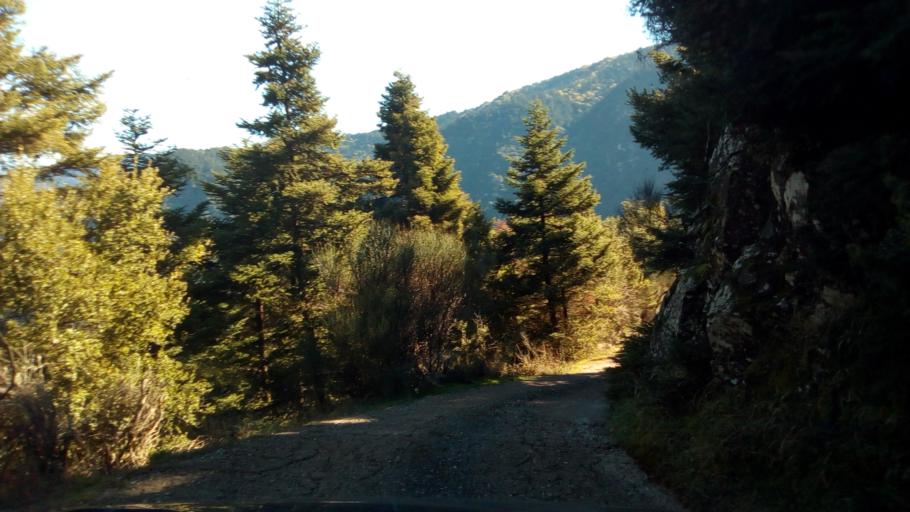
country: GR
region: West Greece
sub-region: Nomos Aitolias kai Akarnanias
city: Nafpaktos
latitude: 38.5930
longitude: 21.8777
